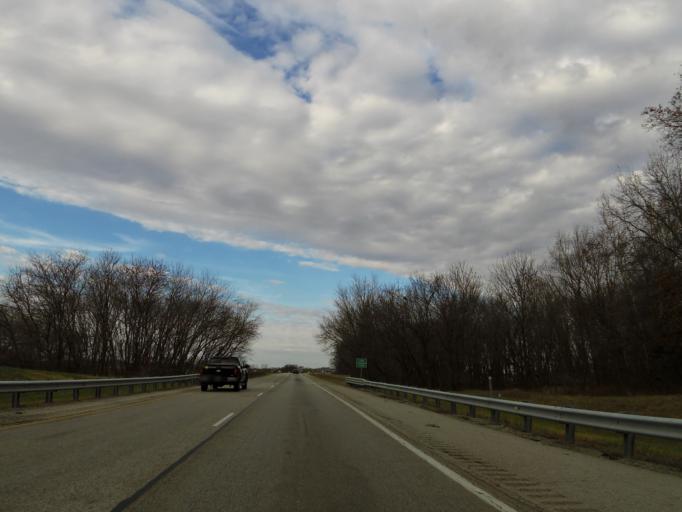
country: US
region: Illinois
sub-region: Washington County
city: Nashville
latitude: 38.4108
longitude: -89.4255
